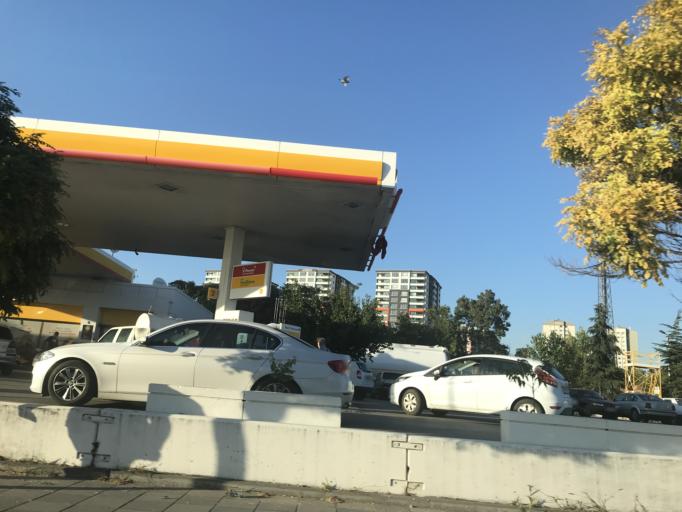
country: TR
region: Ankara
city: Etimesgut
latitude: 39.9654
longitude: 32.6387
